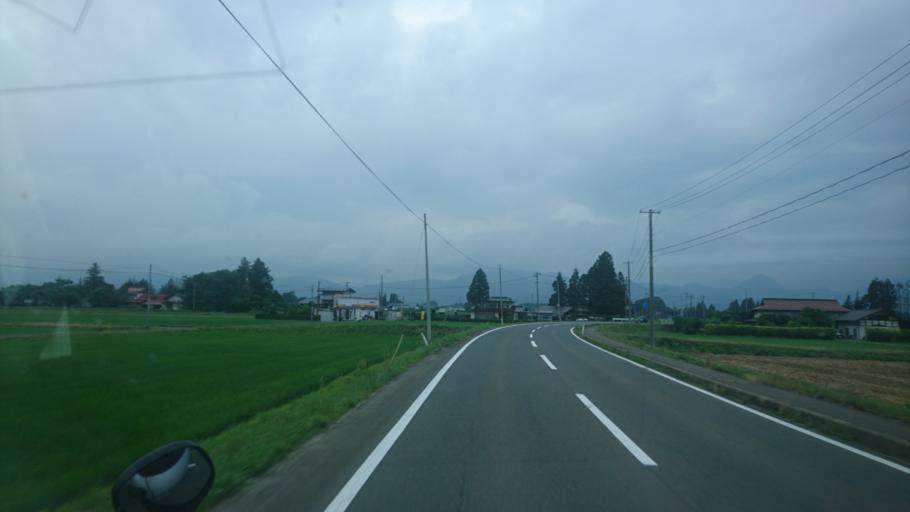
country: JP
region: Iwate
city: Morioka-shi
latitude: 39.5915
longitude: 141.1662
